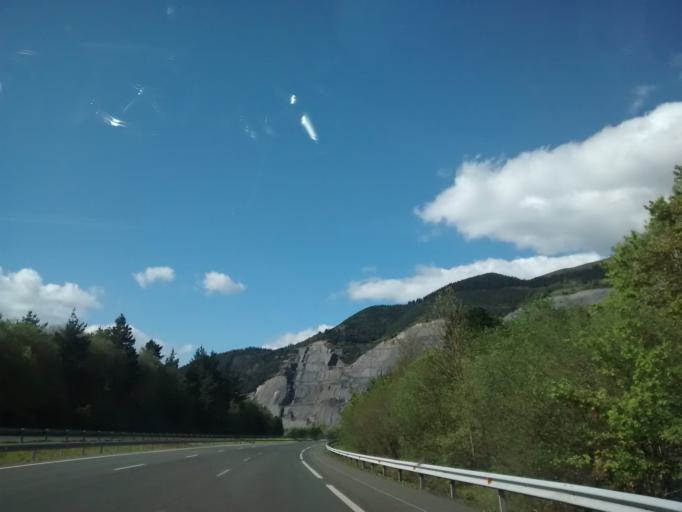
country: ES
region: Basque Country
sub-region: Bizkaia
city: Elexalde
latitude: 43.1174
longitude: -2.9153
